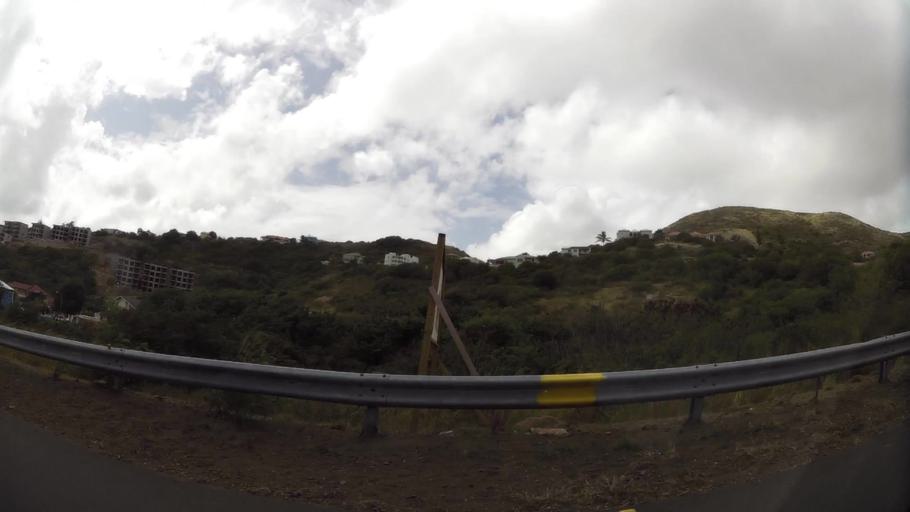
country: KN
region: Saint George Basseterre
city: Basseterre
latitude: 17.2920
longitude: -62.6950
